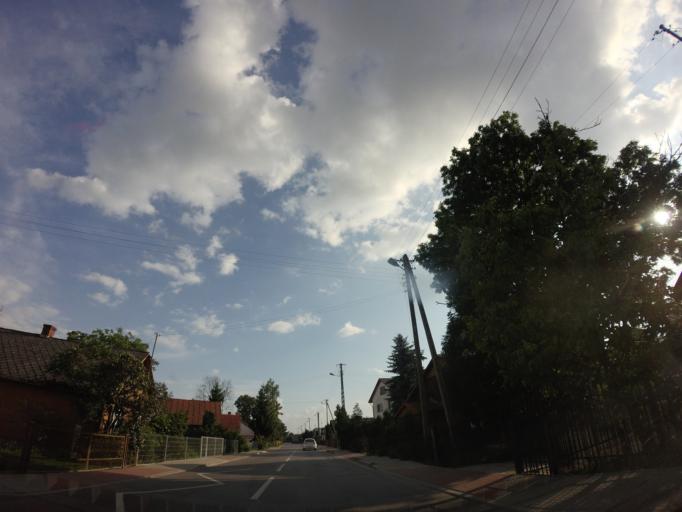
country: PL
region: Lublin Voivodeship
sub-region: Powiat lubartowski
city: Jeziorzany
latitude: 51.6047
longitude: 22.2777
